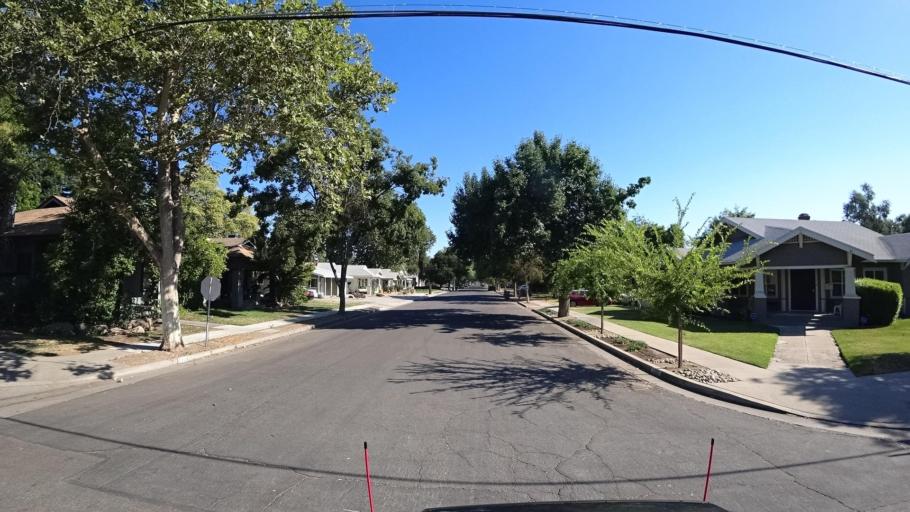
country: US
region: California
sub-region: Fresno County
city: Fresno
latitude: 36.7595
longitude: -119.8097
